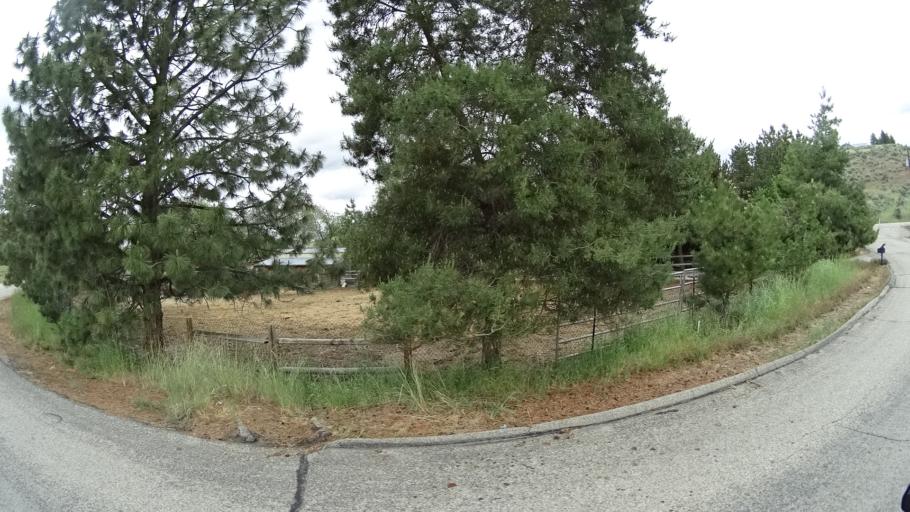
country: US
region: Idaho
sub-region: Ada County
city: Eagle
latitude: 43.7185
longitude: -116.3151
